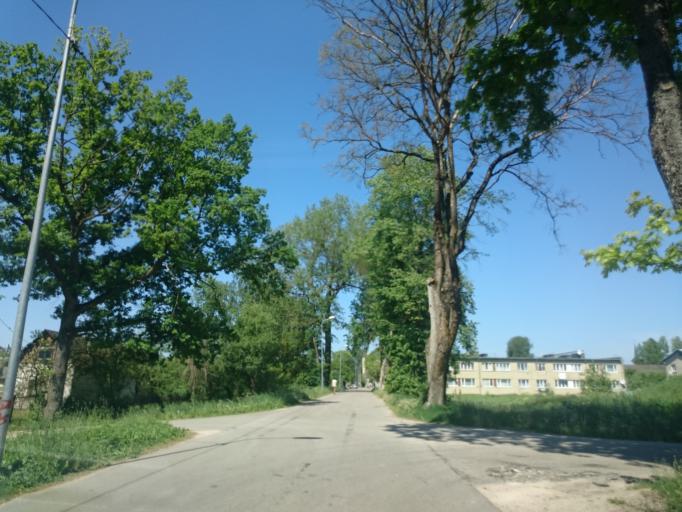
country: LV
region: Olaine
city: Olaine
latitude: 56.7848
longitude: 23.9470
